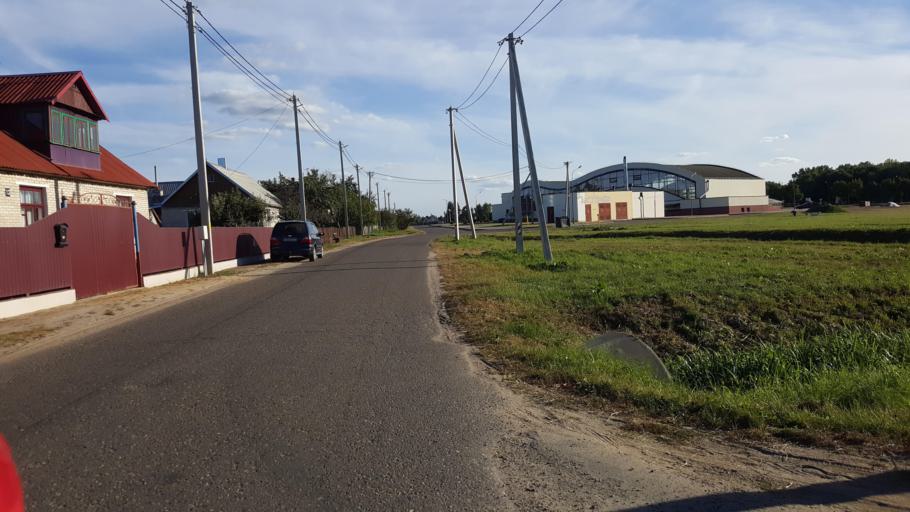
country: BY
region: Brest
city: Kamyanyets
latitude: 52.4014
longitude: 23.8134
